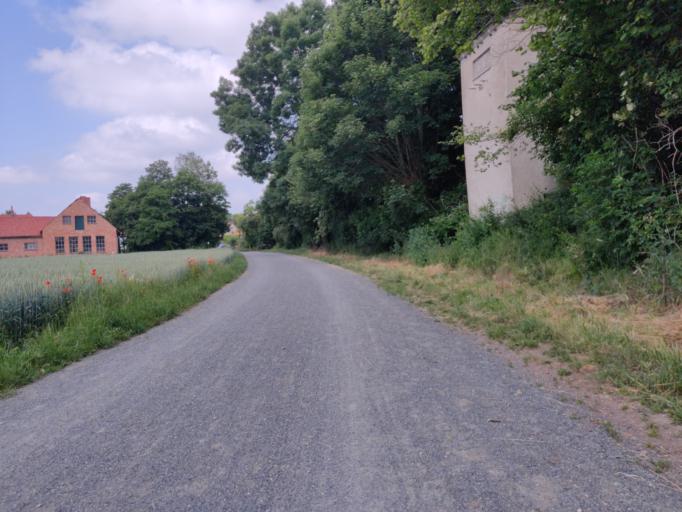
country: DE
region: Lower Saxony
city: Hildesheim
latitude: 52.1137
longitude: 9.9819
